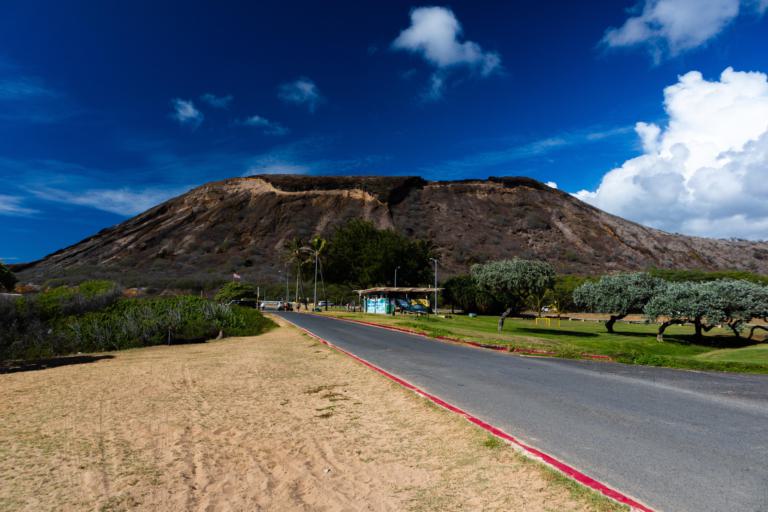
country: US
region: Hawaii
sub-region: Honolulu County
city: Waimanalo Beach
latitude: 21.2861
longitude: -157.6716
